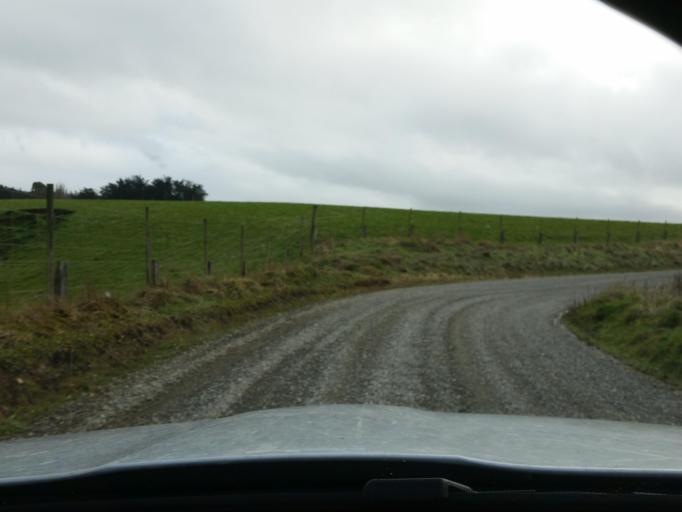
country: NZ
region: Southland
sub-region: Southland District
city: Riverton
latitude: -46.0661
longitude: 167.7743
